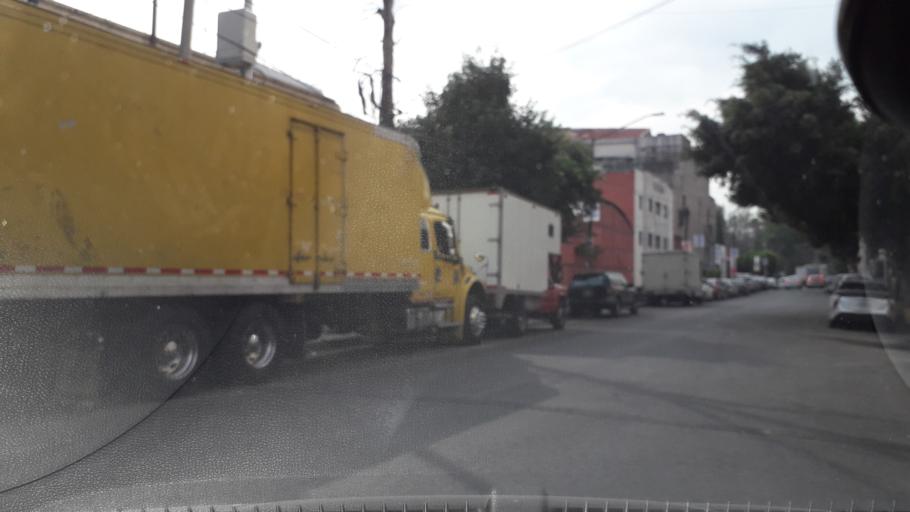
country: MX
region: Mexico City
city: Mexico City
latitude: 19.4202
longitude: -99.1448
